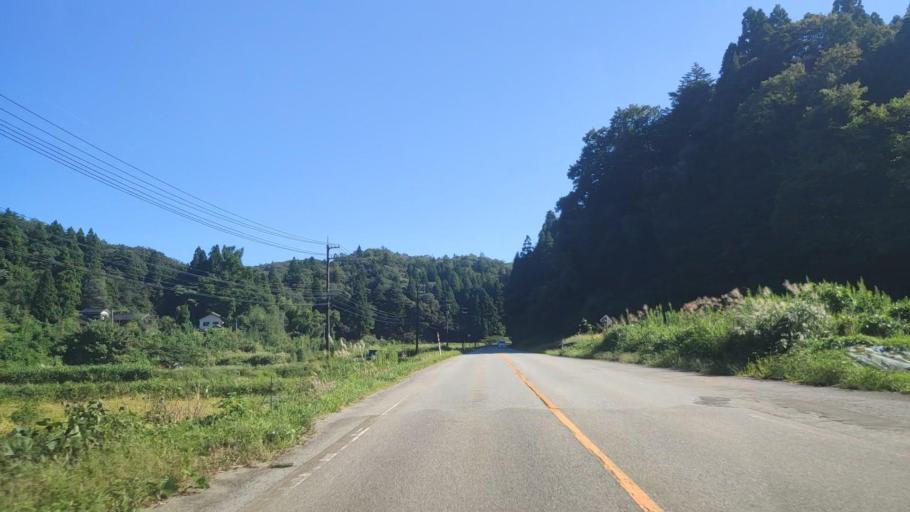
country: JP
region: Ishikawa
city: Nanao
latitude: 37.3328
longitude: 137.2076
